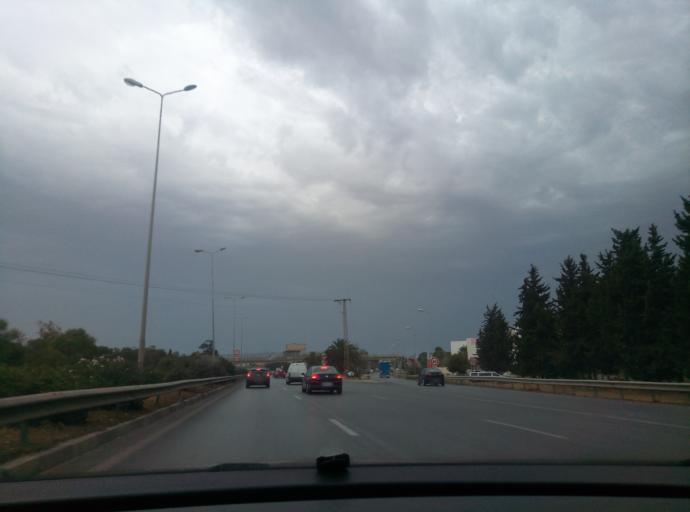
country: TN
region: Bin 'Arus
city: Ben Arous
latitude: 36.7436
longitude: 10.2126
